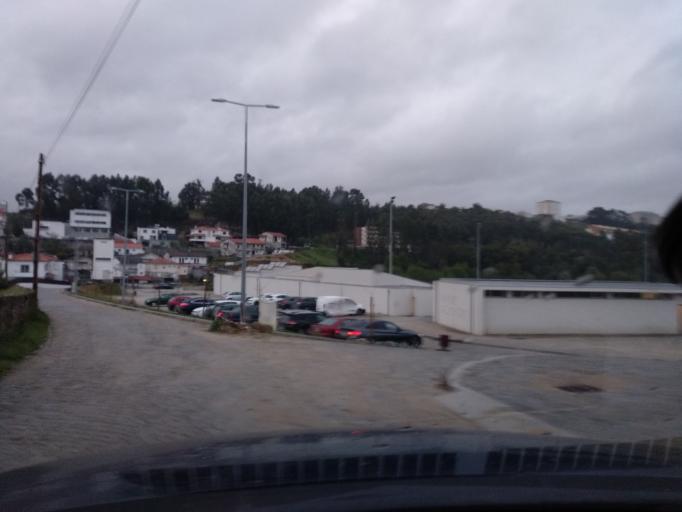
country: PT
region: Porto
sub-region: Penafiel
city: Penafiel
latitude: 41.1904
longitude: -8.2933
